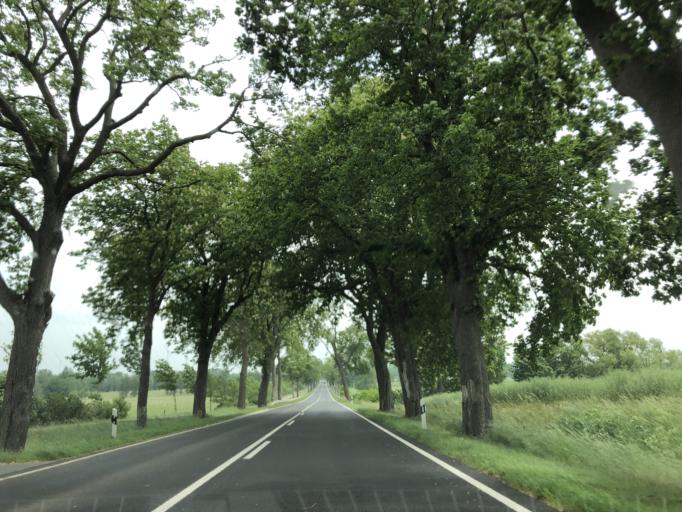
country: DE
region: Brandenburg
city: Gumtow
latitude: 52.9754
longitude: 12.2705
